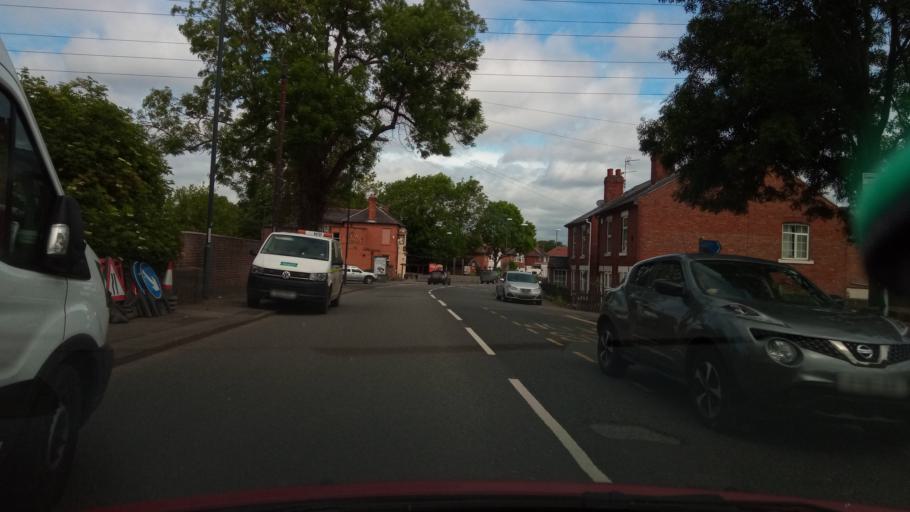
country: GB
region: England
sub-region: Derby
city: Derby
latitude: 52.8776
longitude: -1.4442
